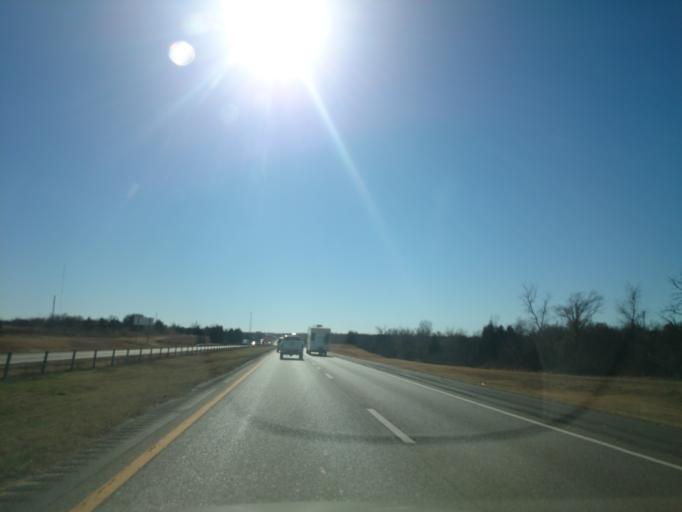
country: US
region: Oklahoma
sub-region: Oklahoma County
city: Edmond
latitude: 35.7091
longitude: -97.4163
